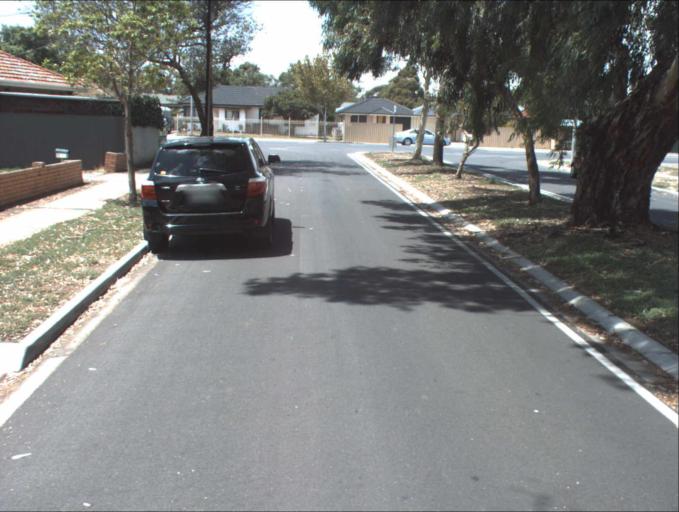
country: AU
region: South Australia
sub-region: Port Adelaide Enfield
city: Enfield
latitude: -34.8534
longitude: 138.6171
